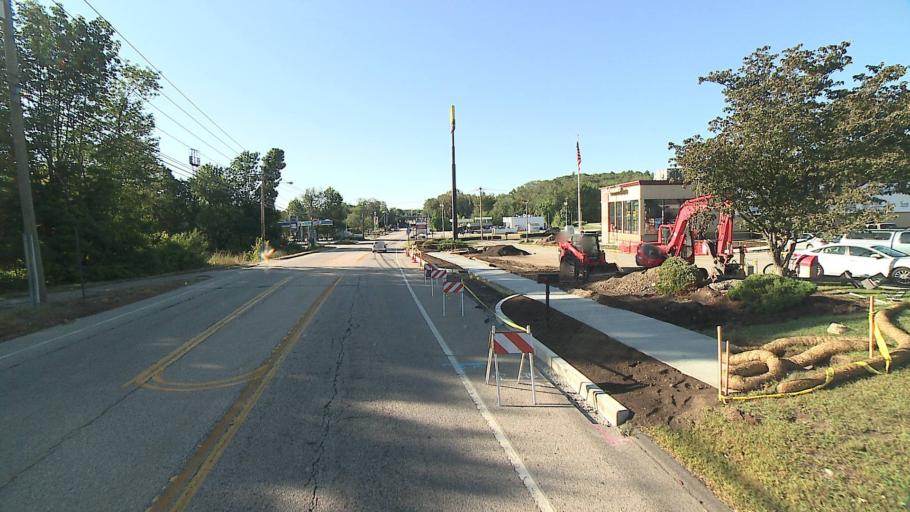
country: US
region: Connecticut
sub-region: New London County
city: Jewett City
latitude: 41.5923
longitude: -71.9911
